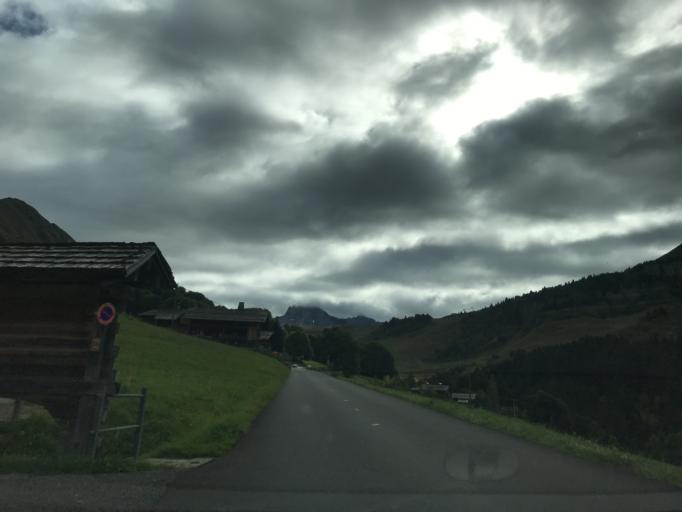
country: FR
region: Rhone-Alpes
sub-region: Departement de la Haute-Savoie
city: Le Grand-Bornand
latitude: 45.9784
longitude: 6.4636
